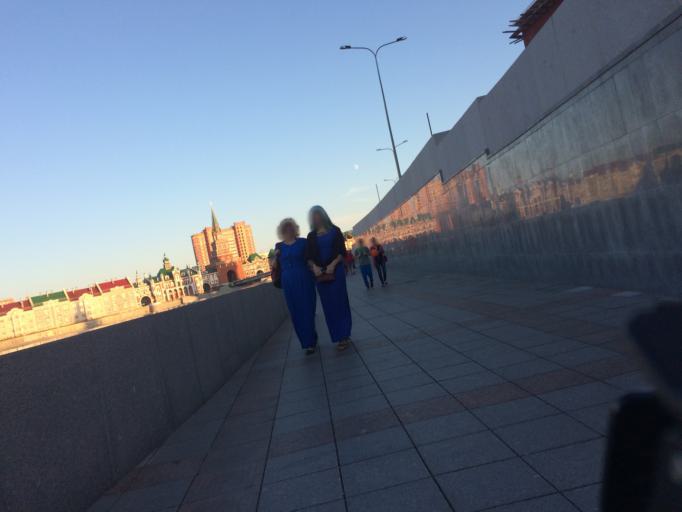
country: RU
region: Mariy-El
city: Yoshkar-Ola
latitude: 56.6350
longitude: 47.9044
